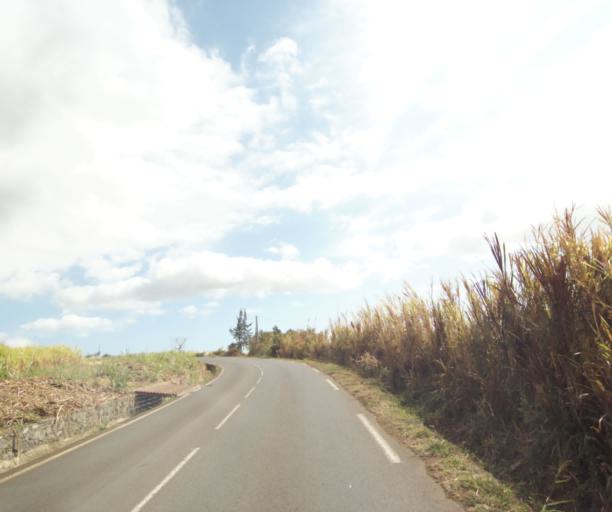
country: RE
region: Reunion
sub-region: Reunion
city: Saint-Paul
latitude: -21.0319
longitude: 55.2865
